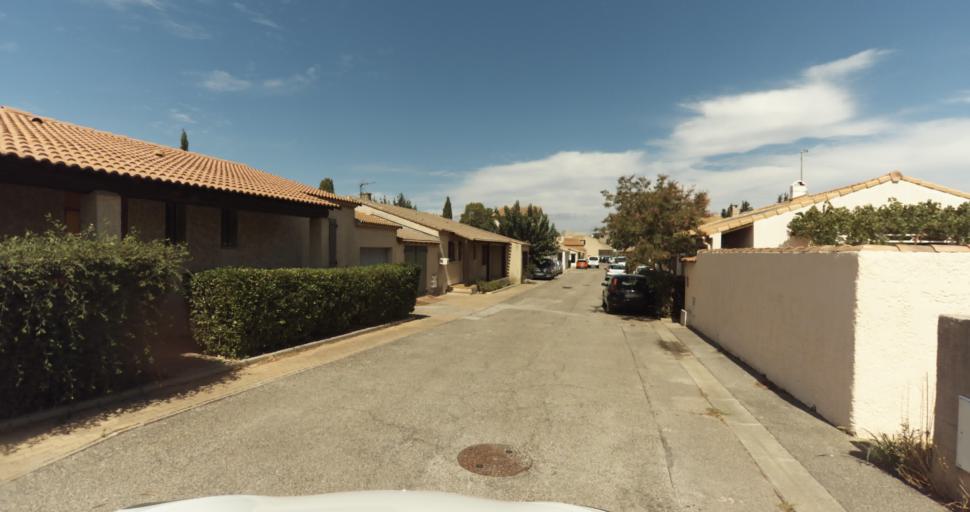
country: FR
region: Provence-Alpes-Cote d'Azur
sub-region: Departement des Bouches-du-Rhone
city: Miramas
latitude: 43.5808
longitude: 5.0159
